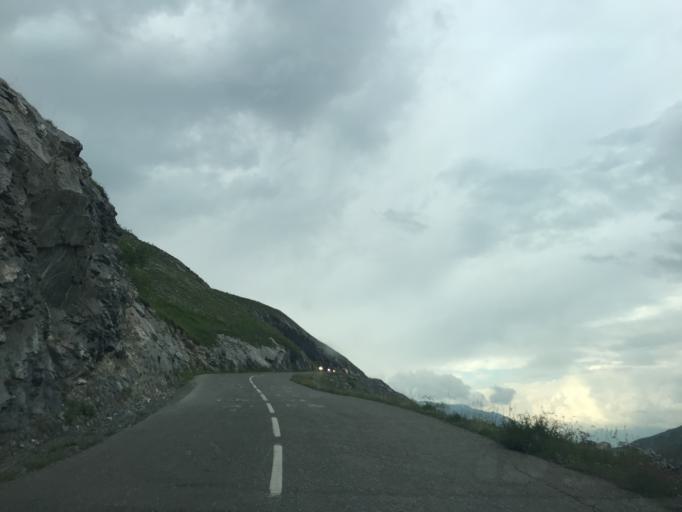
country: FR
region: Rhone-Alpes
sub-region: Departement de la Savoie
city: Valloire
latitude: 45.0885
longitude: 6.4324
